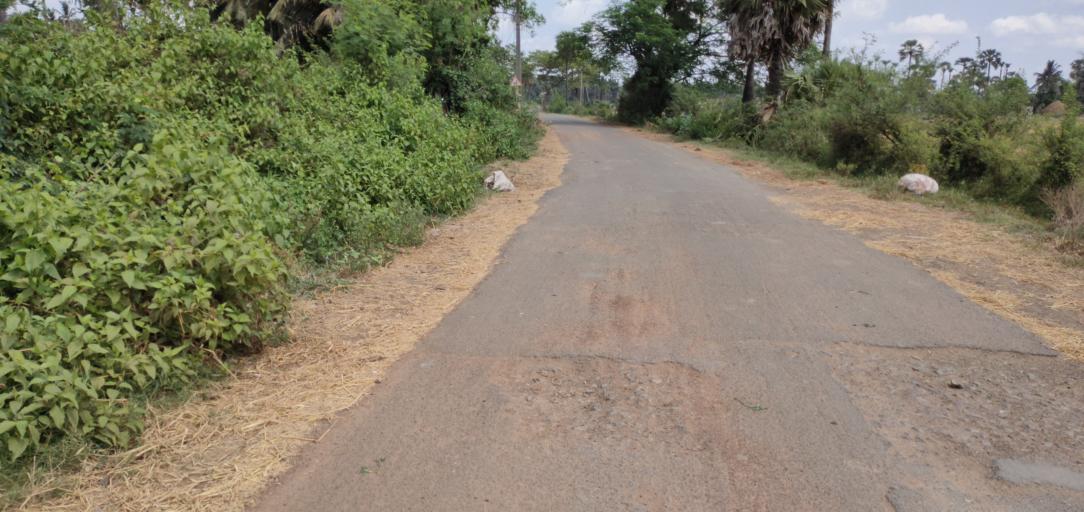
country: IN
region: Andhra Pradesh
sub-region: West Godavari
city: Tadepallegudem
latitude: 16.8502
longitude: 81.4950
